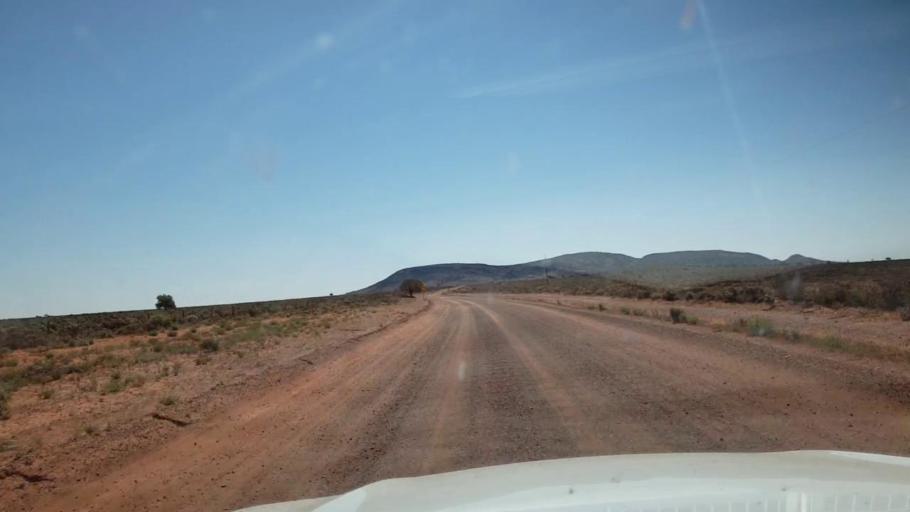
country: AU
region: South Australia
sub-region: Whyalla
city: Whyalla
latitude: -32.7112
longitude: 137.1407
